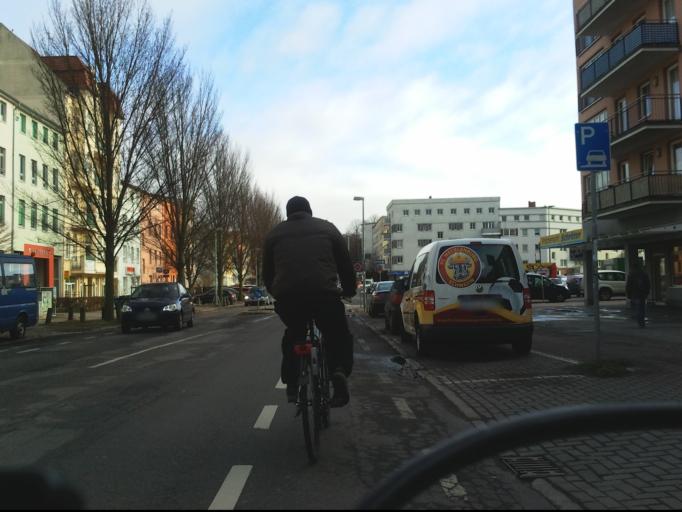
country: DE
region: Mecklenburg-Vorpommern
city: Rostock
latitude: 54.0864
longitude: 12.1122
